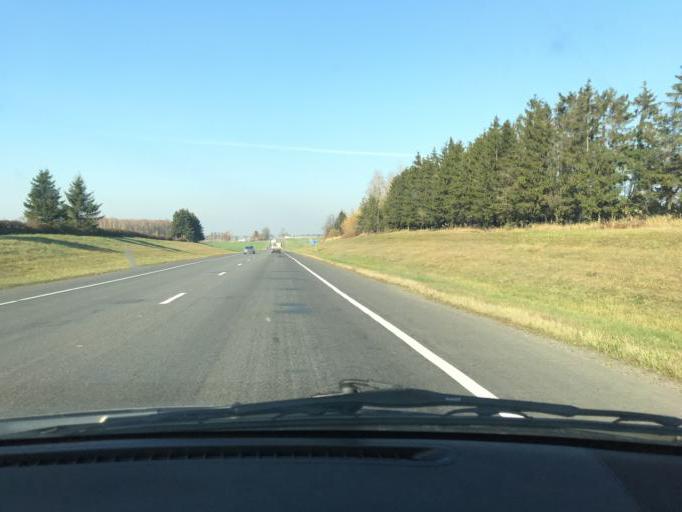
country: BY
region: Mogilev
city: Shklow
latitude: 54.2267
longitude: 30.4521
